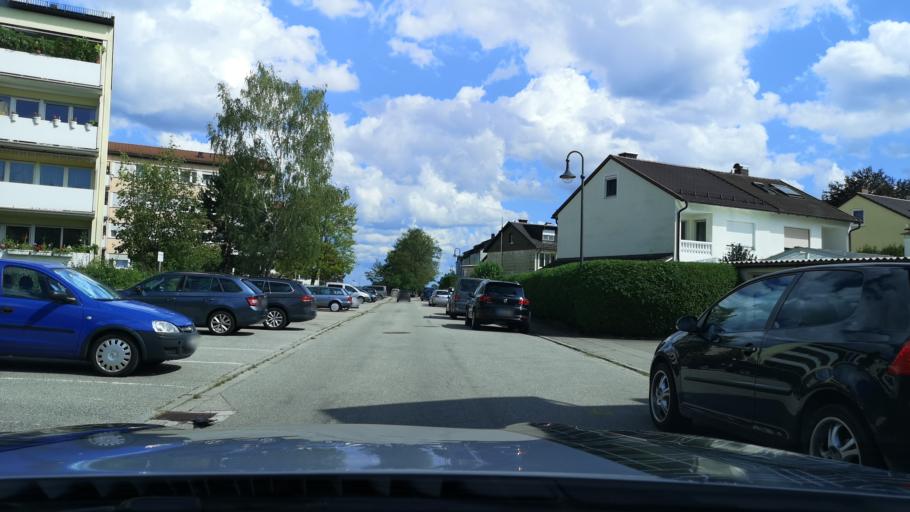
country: DE
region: Bavaria
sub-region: Upper Bavaria
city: Garching bei Munchen
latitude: 48.2466
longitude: 11.6132
